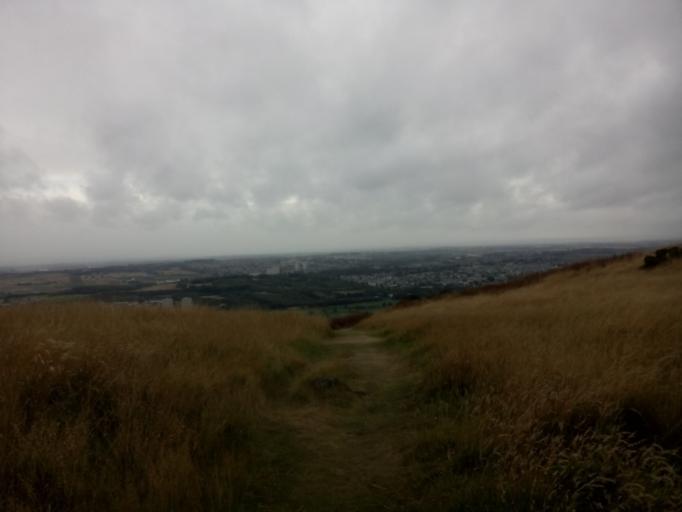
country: GB
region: Scotland
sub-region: West Lothian
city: Seafield
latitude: 55.9426
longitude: -3.1601
